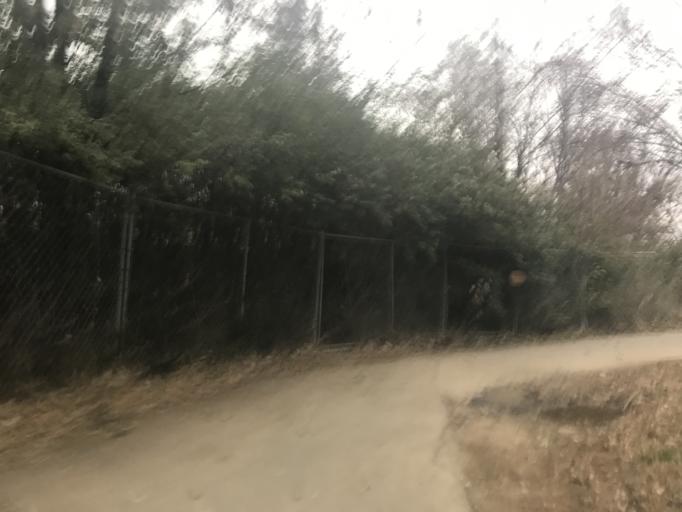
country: US
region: Indiana
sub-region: Clark County
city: Jeffersonville
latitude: 38.2661
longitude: -85.7219
